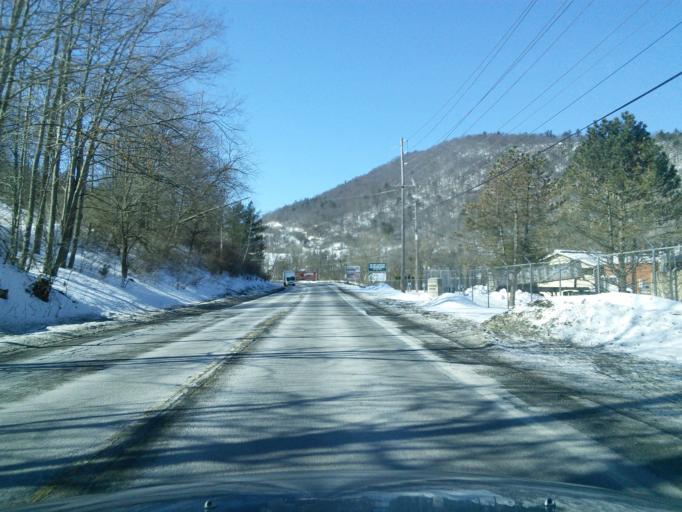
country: US
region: Pennsylvania
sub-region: Centre County
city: Bellefonte
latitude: 40.9222
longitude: -77.7831
